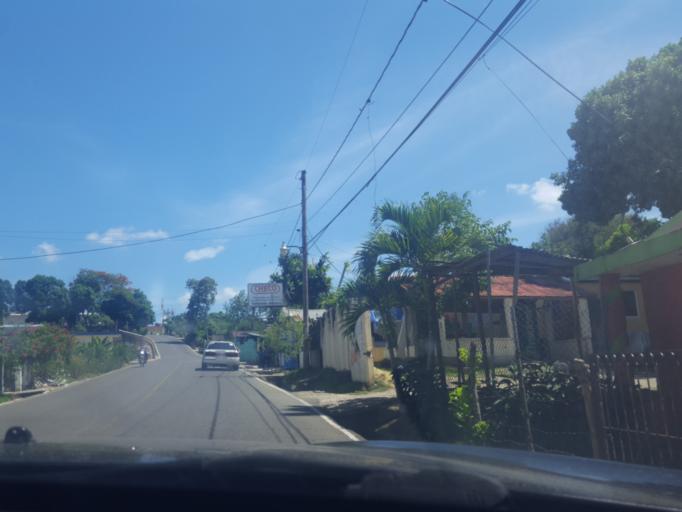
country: DO
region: Santiago
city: Licey al Medio
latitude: 19.3866
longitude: -70.6500
